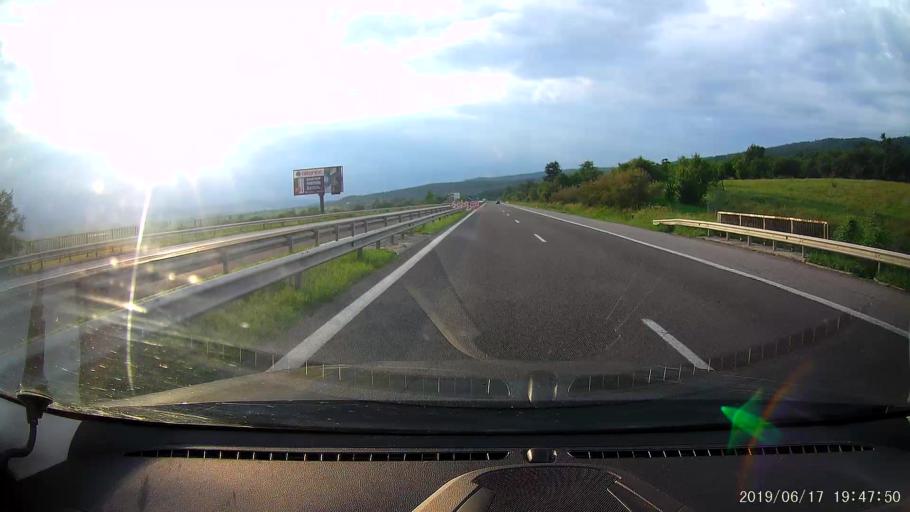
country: BG
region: Sofiya
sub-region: Obshtina Ikhtiman
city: Ikhtiman
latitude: 42.4565
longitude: 23.8373
